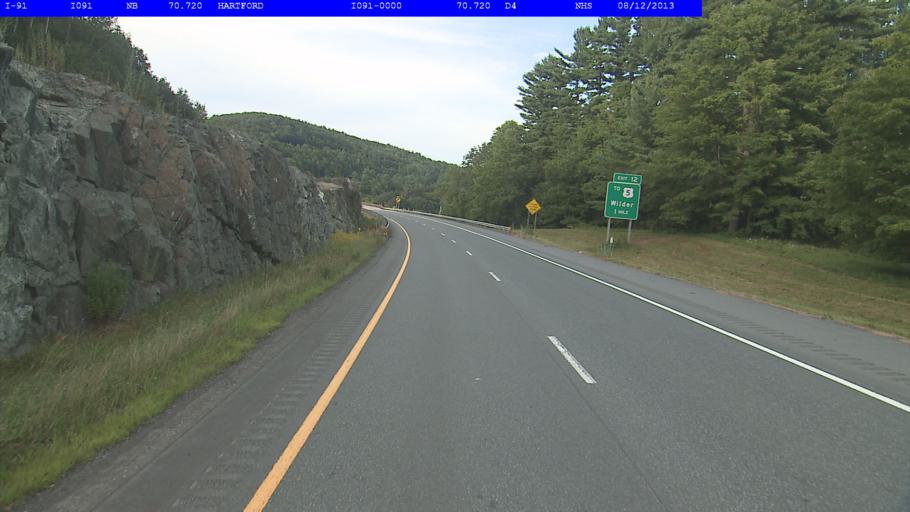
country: US
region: Vermont
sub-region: Windsor County
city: White River Junction
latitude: 43.6516
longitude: -72.3324
